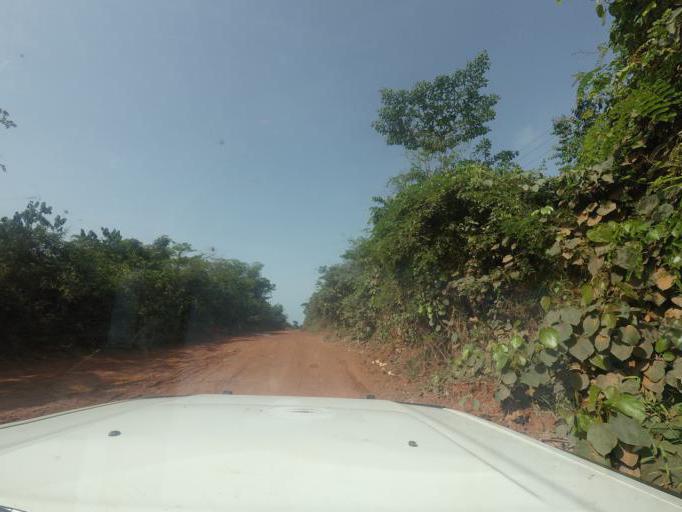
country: LR
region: Nimba
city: Sanniquellie
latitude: 7.1757
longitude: -8.9685
